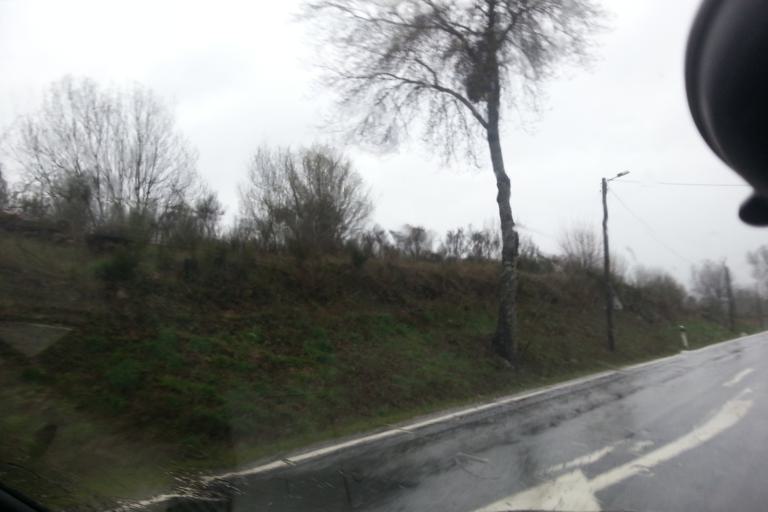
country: PT
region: Guarda
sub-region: Fornos de Algodres
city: Fornos de Algodres
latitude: 40.5424
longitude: -7.5353
